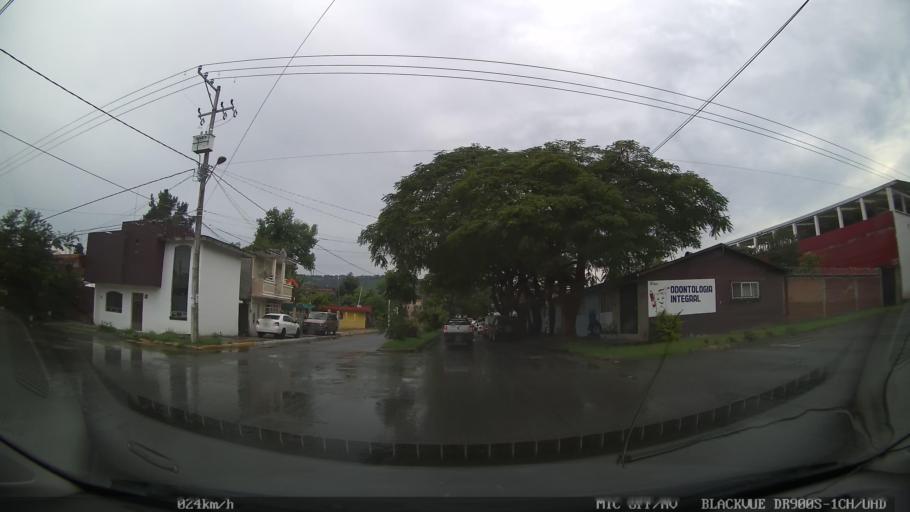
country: MX
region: Michoacan
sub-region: Uruapan
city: Santa Rosa (Santa Barbara)
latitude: 19.3893
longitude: -102.0558
